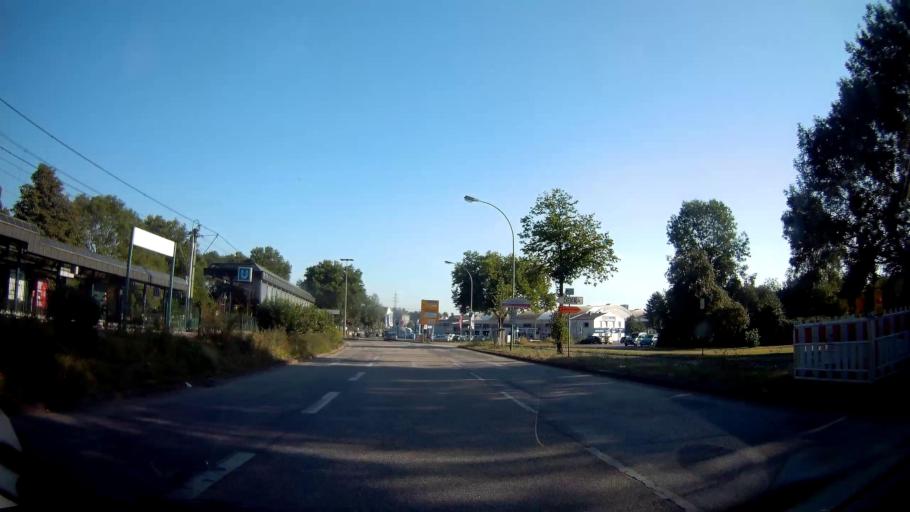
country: DE
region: North Rhine-Westphalia
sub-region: Regierungsbezirk Arnsberg
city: Dortmund
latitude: 51.5359
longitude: 7.4568
